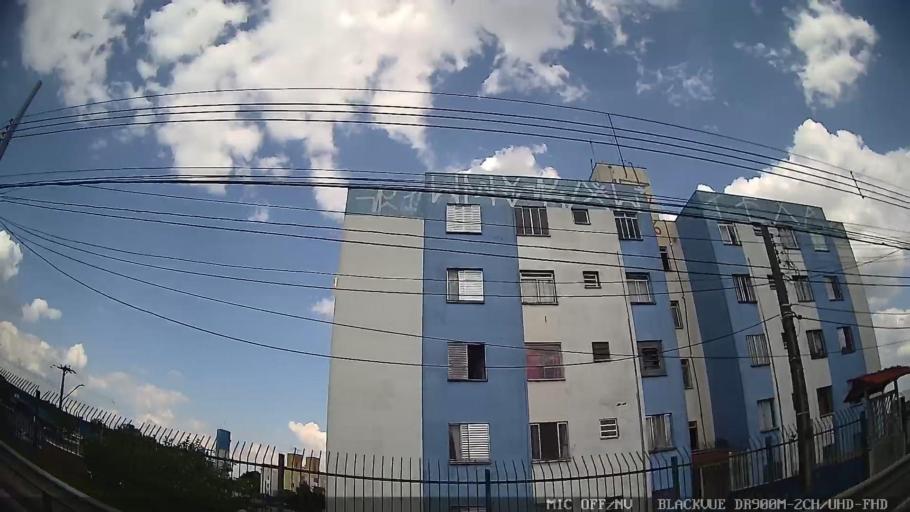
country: BR
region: Sao Paulo
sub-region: Guarulhos
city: Guarulhos
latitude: -23.5026
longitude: -46.4713
